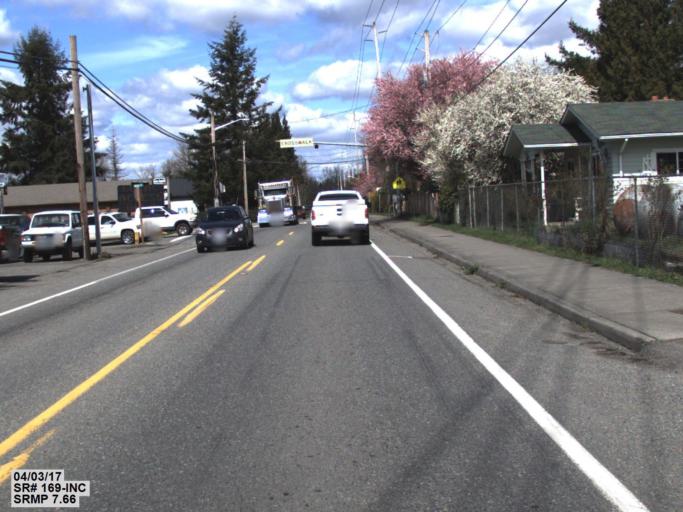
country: US
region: Washington
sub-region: King County
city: Black Diamond
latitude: 47.3091
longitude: -122.0035
